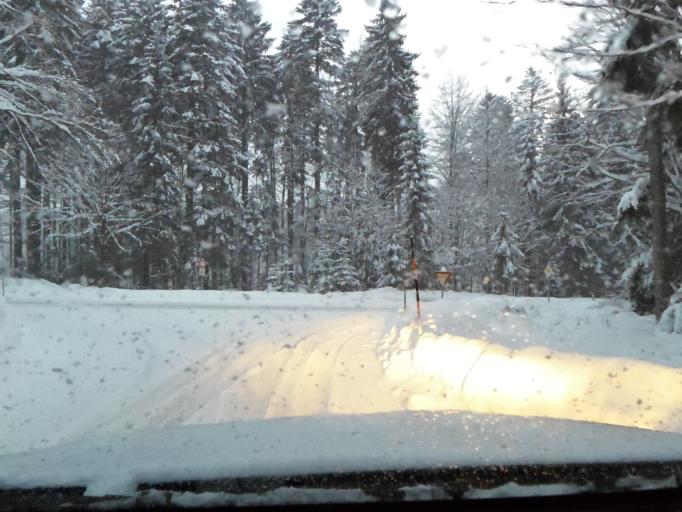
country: DE
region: Bavaria
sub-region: Lower Bavaria
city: Spiegelau
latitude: 48.9238
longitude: 13.4171
